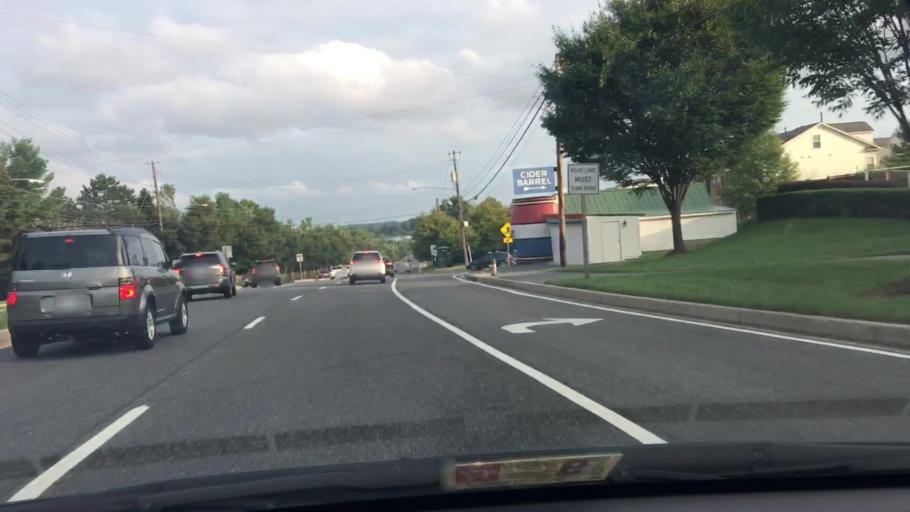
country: US
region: Maryland
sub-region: Montgomery County
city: Germantown
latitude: 39.1905
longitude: -77.2420
